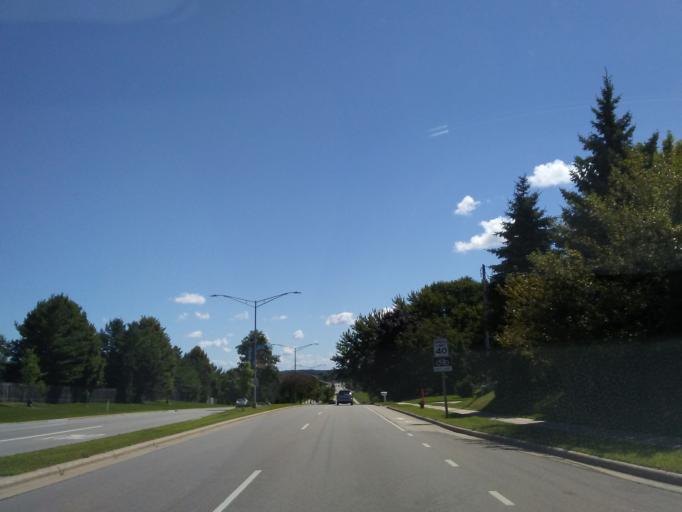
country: US
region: Wisconsin
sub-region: Dane County
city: Shorewood Hills
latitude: 43.0155
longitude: -89.4399
